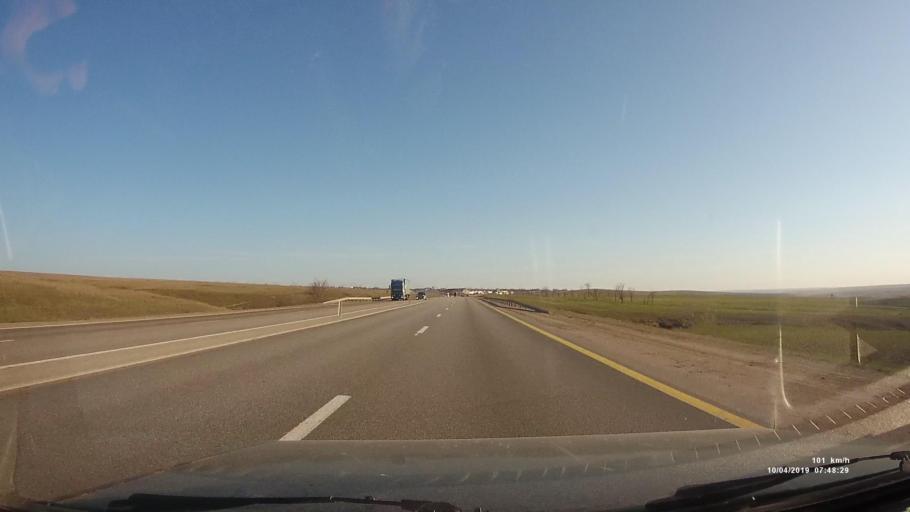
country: RU
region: Rostov
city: Kamensk-Shakhtinskiy
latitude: 48.2346
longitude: 40.2812
